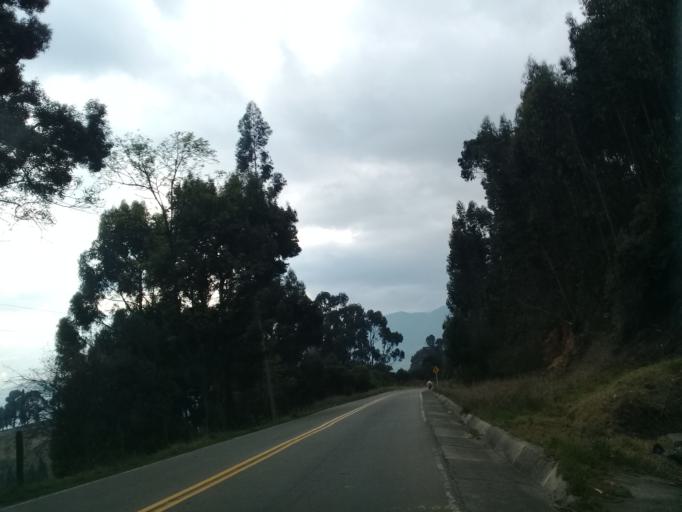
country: CO
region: Cundinamarca
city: Zipaquira
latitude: 5.0305
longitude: -74.0331
